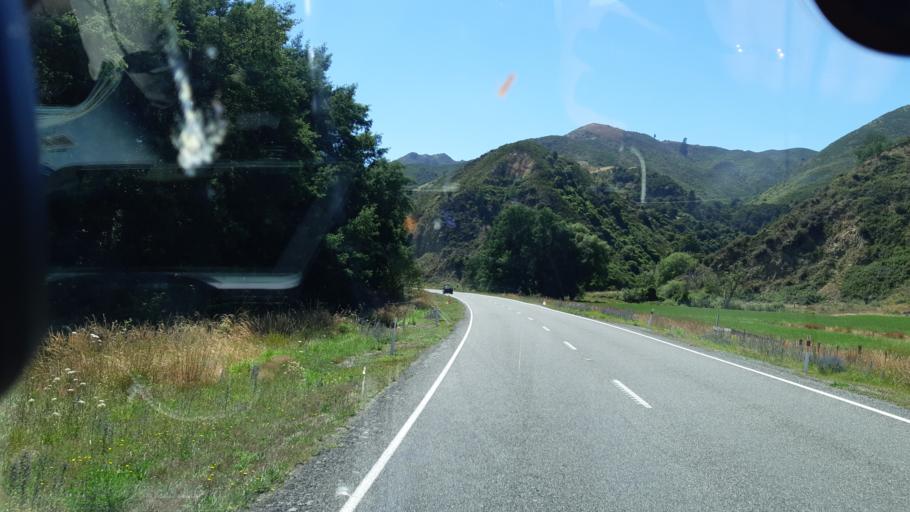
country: NZ
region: Canterbury
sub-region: Kaikoura District
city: Kaikoura
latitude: -42.6369
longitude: 173.3415
